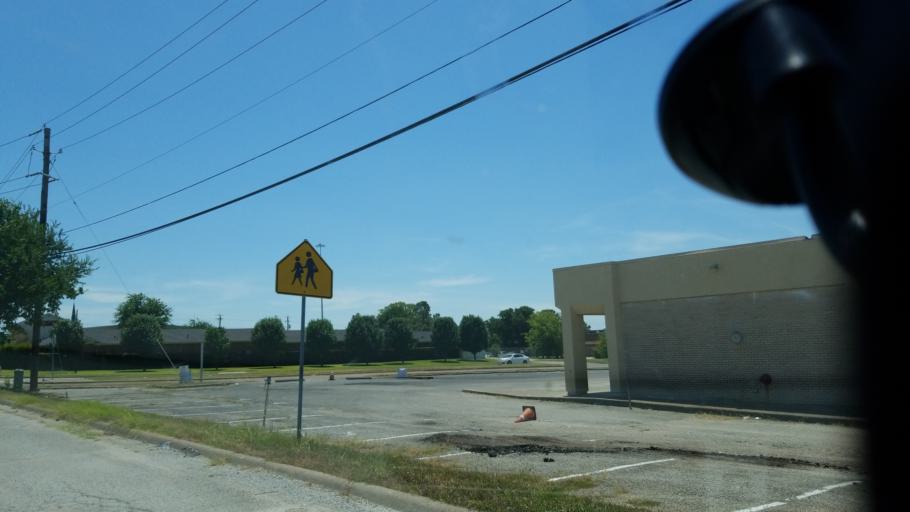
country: US
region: Texas
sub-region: Dallas County
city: Cockrell Hill
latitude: 32.6913
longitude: -96.8256
